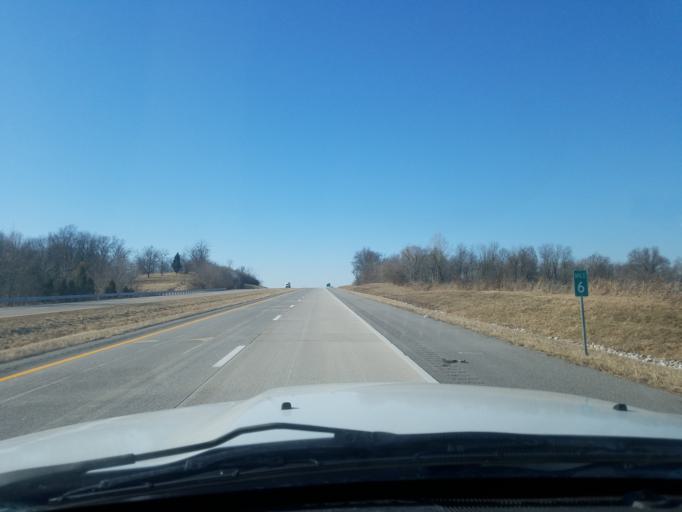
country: US
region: Kentucky
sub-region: Henderson County
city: Henderson
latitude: 37.7828
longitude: -87.4611
